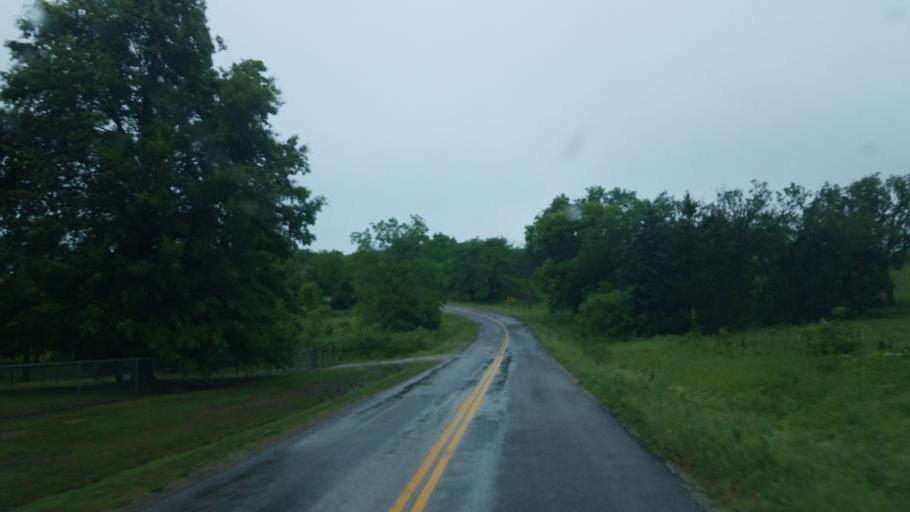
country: US
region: Missouri
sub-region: Moniteau County
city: California
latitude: 38.6864
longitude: -92.5844
